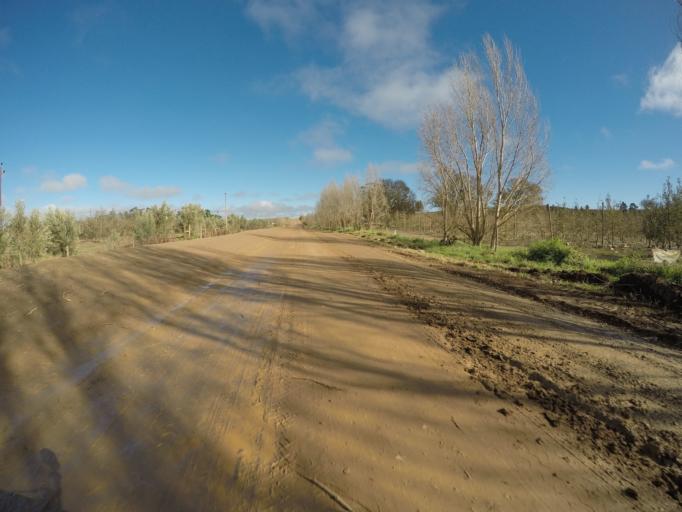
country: ZA
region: Western Cape
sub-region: Overberg District Municipality
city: Caledon
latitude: -34.1116
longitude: 19.7469
